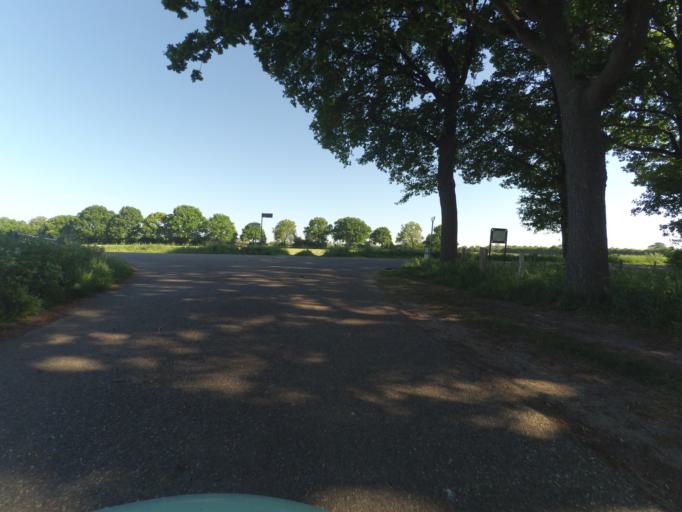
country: NL
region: Gelderland
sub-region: Gemeente Voorst
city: Wilp
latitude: 52.1998
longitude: 6.1567
